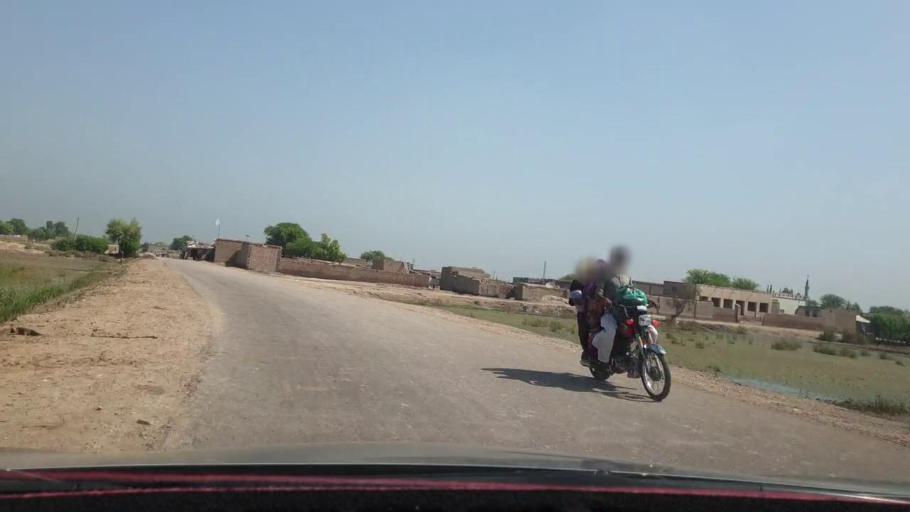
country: PK
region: Sindh
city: Warah
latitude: 27.4751
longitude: 67.8329
